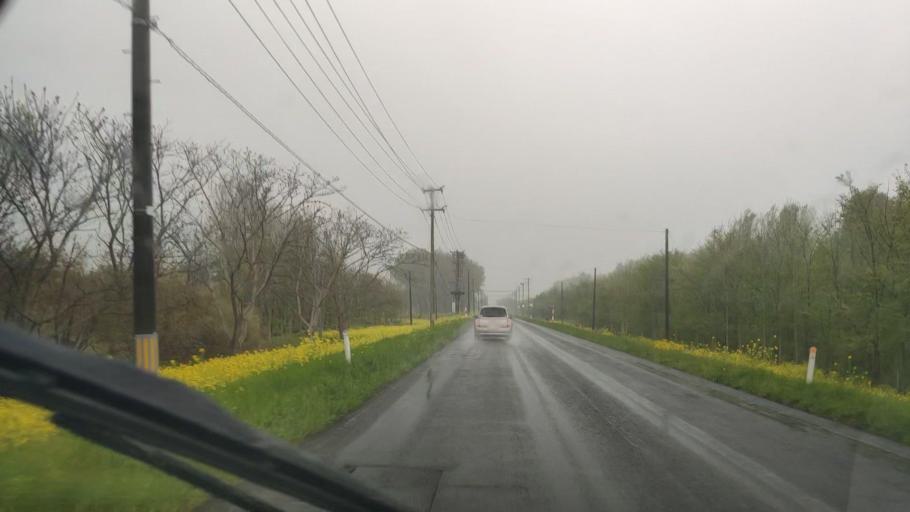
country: JP
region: Akita
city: Tenno
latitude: 39.9510
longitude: 139.9459
